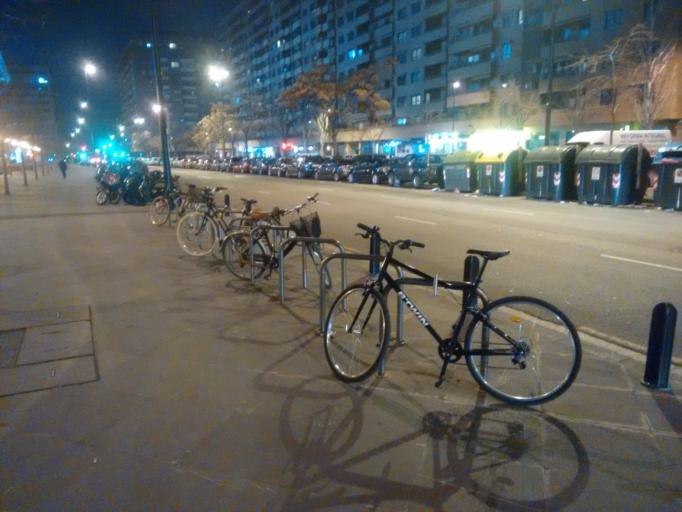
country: ES
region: Aragon
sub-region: Provincia de Zaragoza
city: Delicias
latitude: 41.6395
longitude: -0.9083
